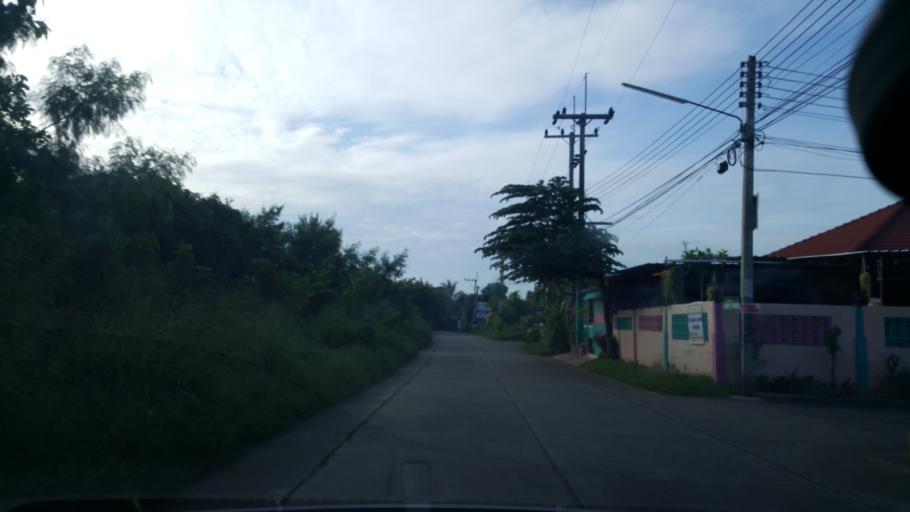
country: TH
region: Chon Buri
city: Sattahip
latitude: 12.6819
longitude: 100.9109
